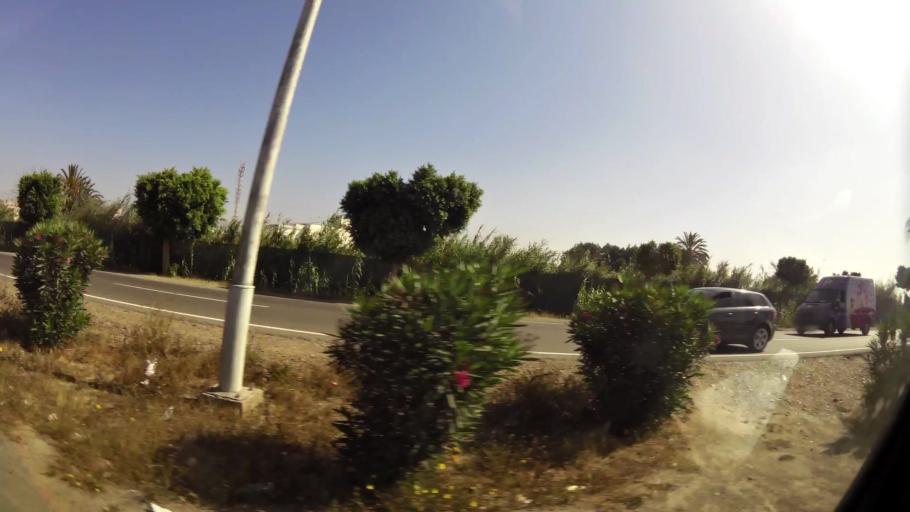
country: MA
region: Souss-Massa-Draa
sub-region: Inezgane-Ait Mellou
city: Inezgane
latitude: 30.3696
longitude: -9.5003
